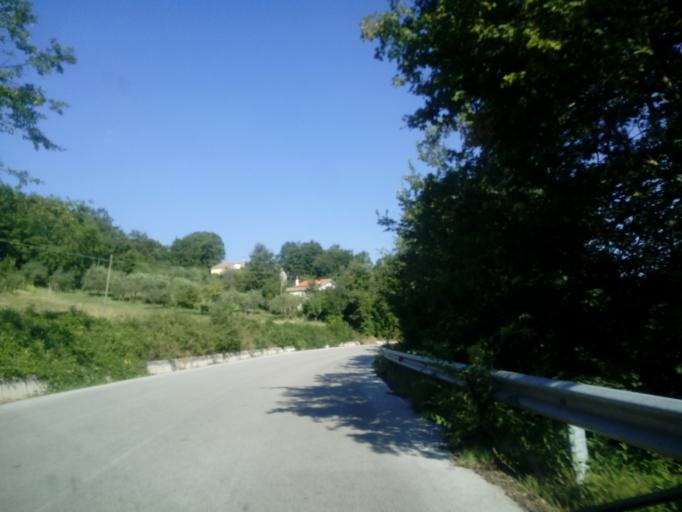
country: IT
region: Molise
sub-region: Provincia di Campobasso
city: Gildone
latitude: 41.5144
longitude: 14.7594
